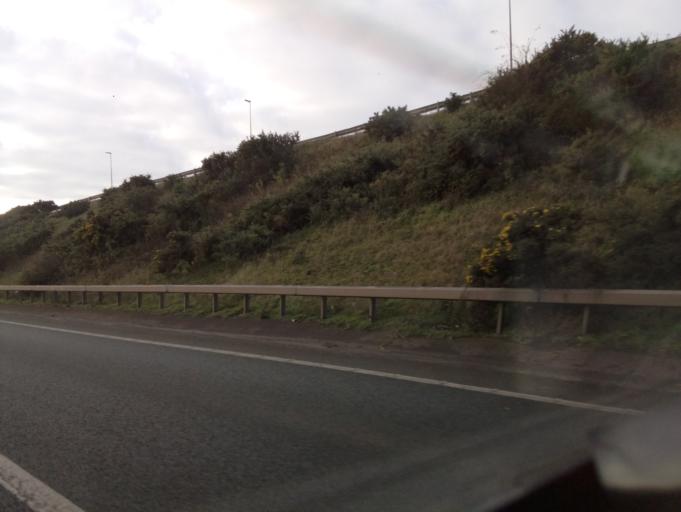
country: GB
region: England
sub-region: Staffordshire
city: Shenstone
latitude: 52.6384
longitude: -1.8039
